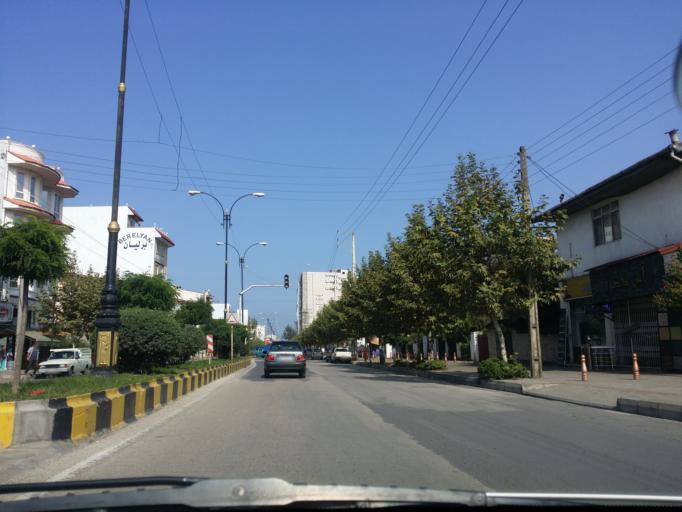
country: IR
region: Mazandaran
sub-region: Nowshahr
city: Nowshahr
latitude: 36.6430
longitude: 51.4914
